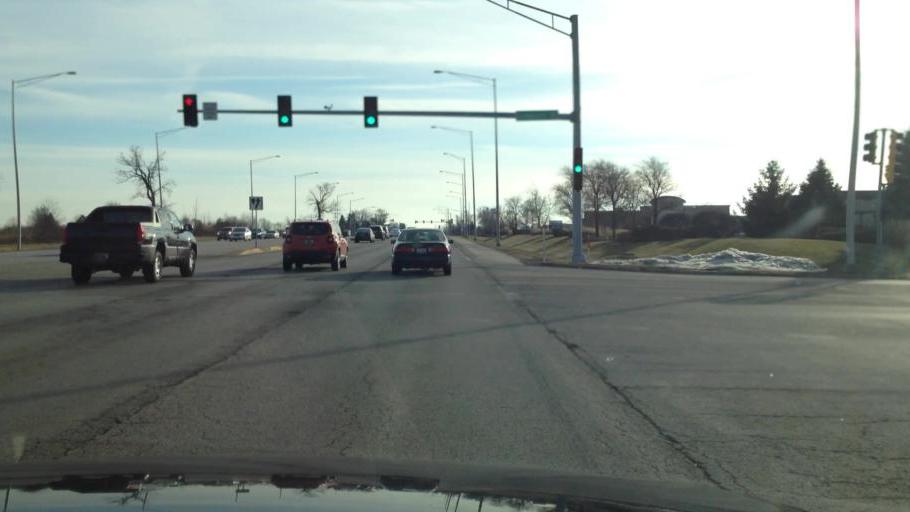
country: US
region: Illinois
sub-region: McHenry County
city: Lake in the Hills
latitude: 42.1506
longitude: -88.3359
